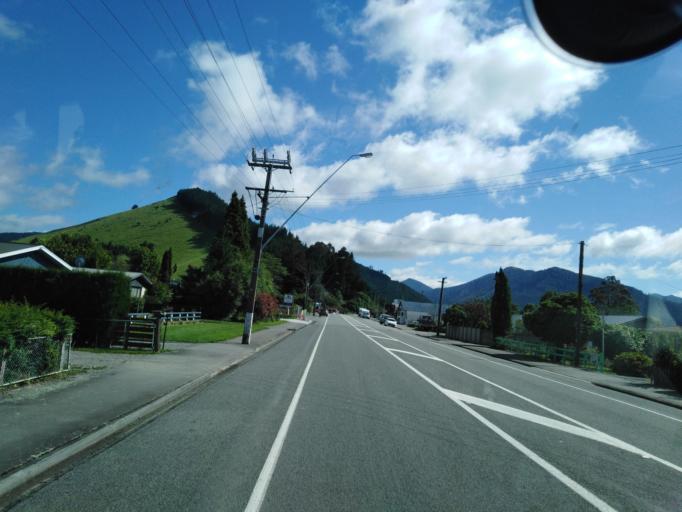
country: NZ
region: Nelson
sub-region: Nelson City
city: Nelson
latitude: -41.2292
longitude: 173.5825
